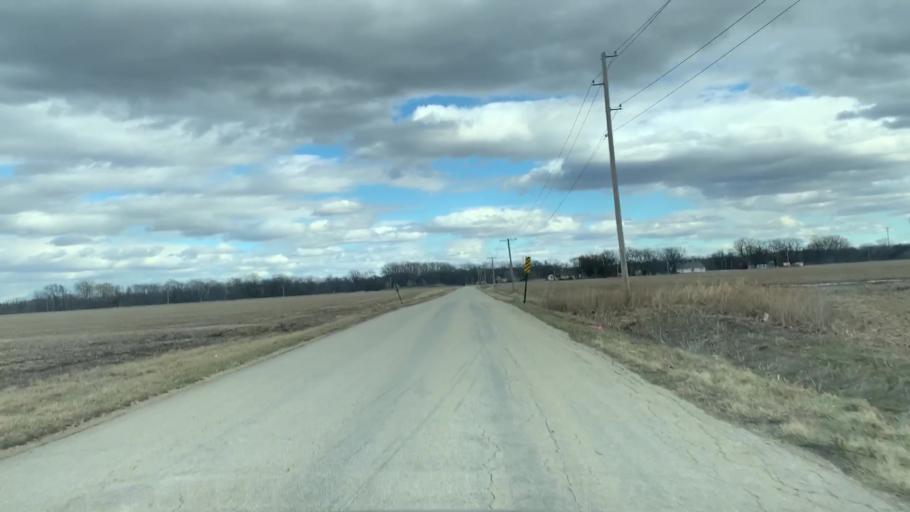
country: US
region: Kansas
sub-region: Allen County
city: Humboldt
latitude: 37.8129
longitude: -95.4588
